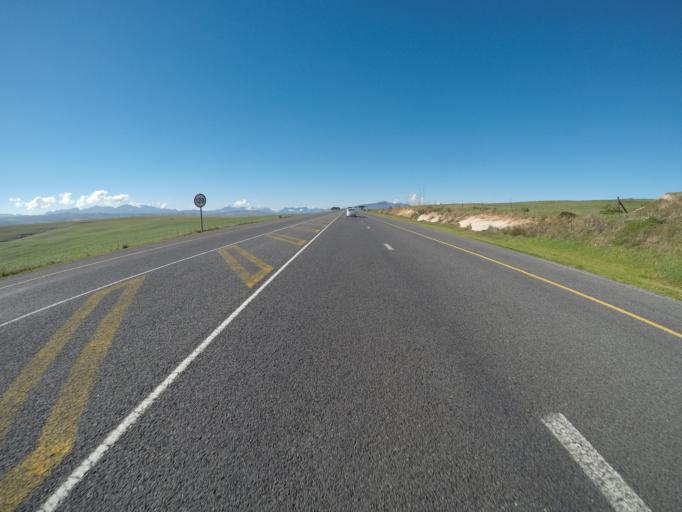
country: ZA
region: Western Cape
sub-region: Overberg District Municipality
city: Caledon
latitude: -34.2246
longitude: 19.2968
